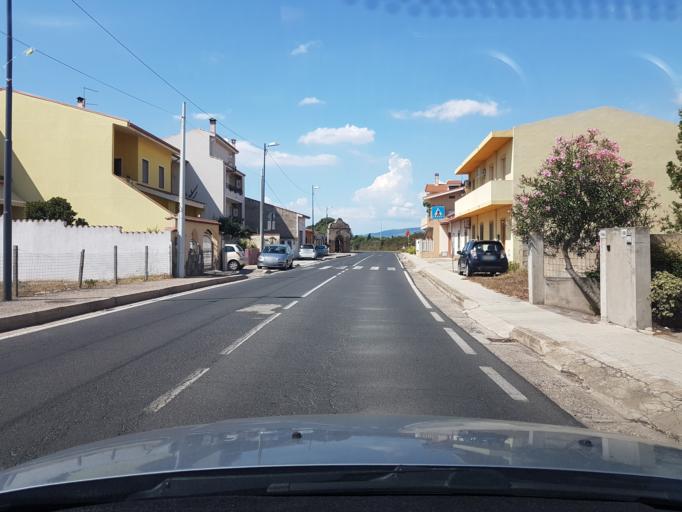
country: IT
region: Sardinia
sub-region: Provincia di Oristano
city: Donigala Fenugheddu
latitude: 39.9372
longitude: 8.5720
